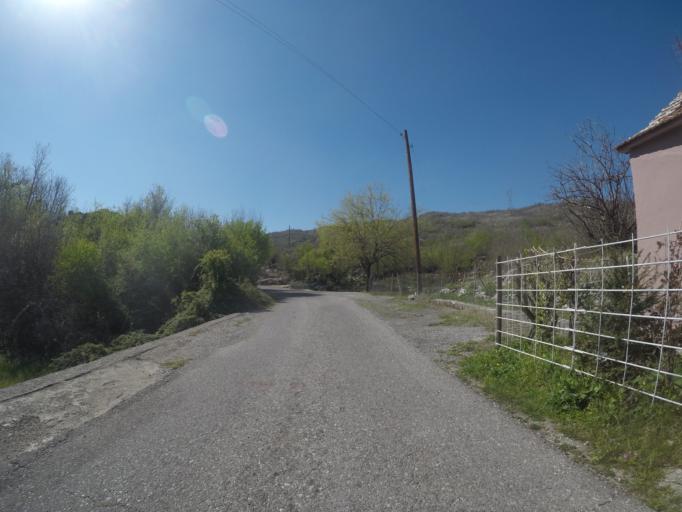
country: ME
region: Danilovgrad
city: Danilovgrad
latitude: 42.5183
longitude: 19.0521
